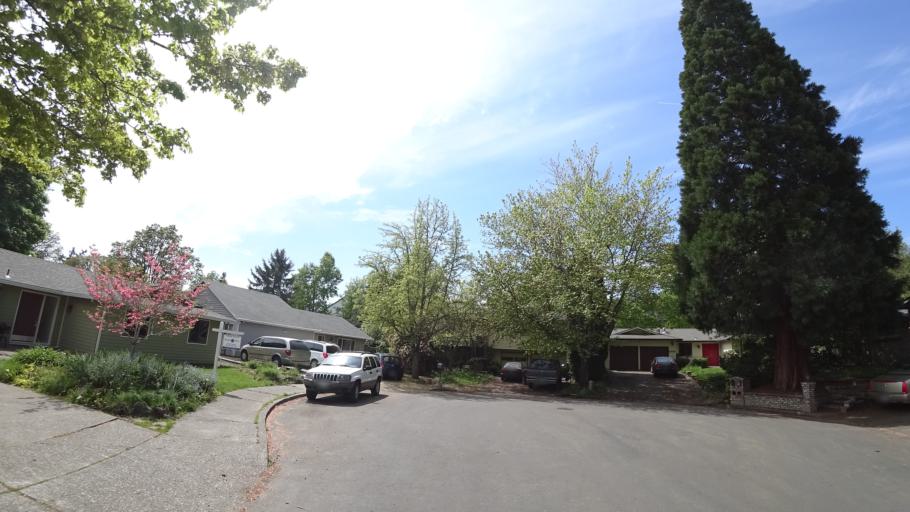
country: US
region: Oregon
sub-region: Washington County
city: Aloha
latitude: 45.4870
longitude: -122.8894
